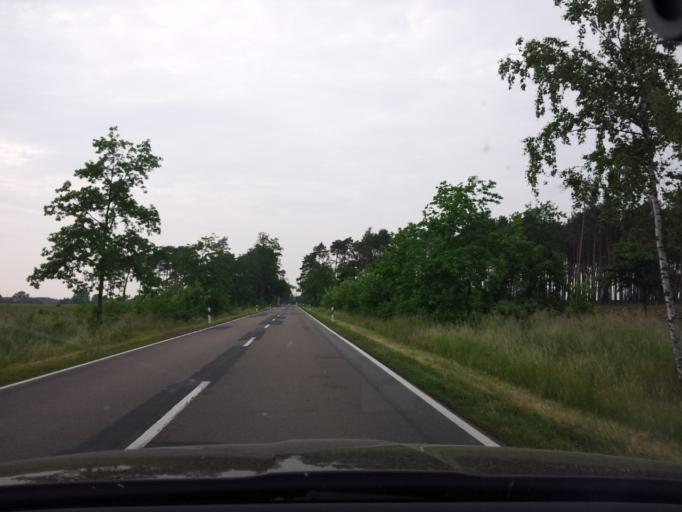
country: DE
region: Brandenburg
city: Linthe
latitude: 52.1256
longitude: 12.8032
